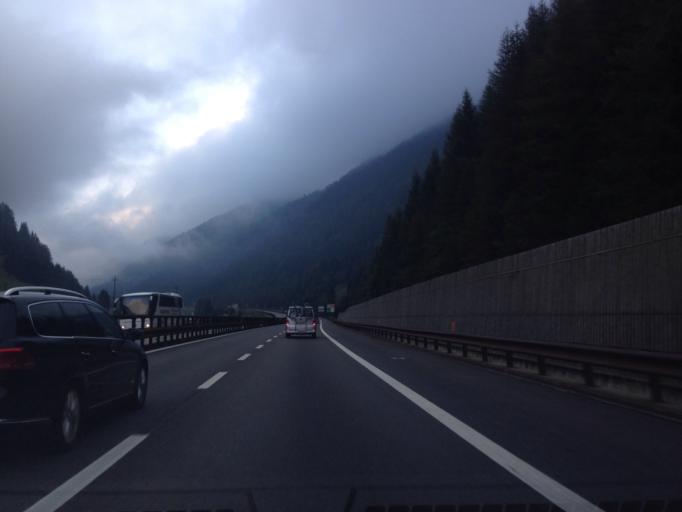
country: IT
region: Trentino-Alto Adige
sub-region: Bolzano
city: Colle Isarco
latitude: 46.9794
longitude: 11.4879
